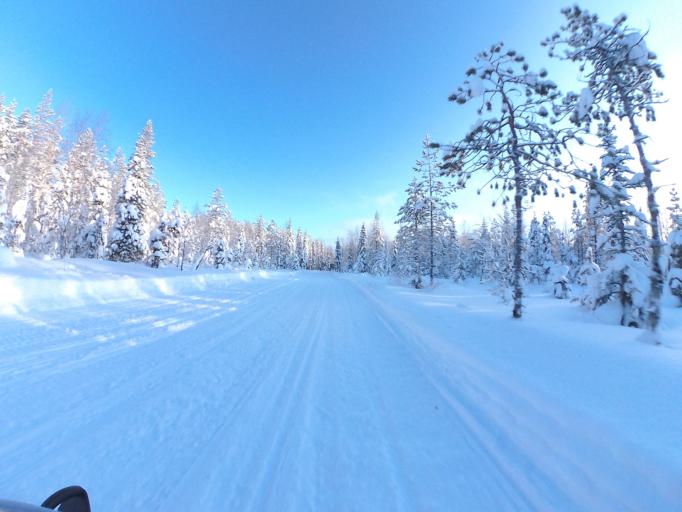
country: FI
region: Lapland
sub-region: Rovaniemi
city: Rovaniemi
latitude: 66.5966
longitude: 25.8558
